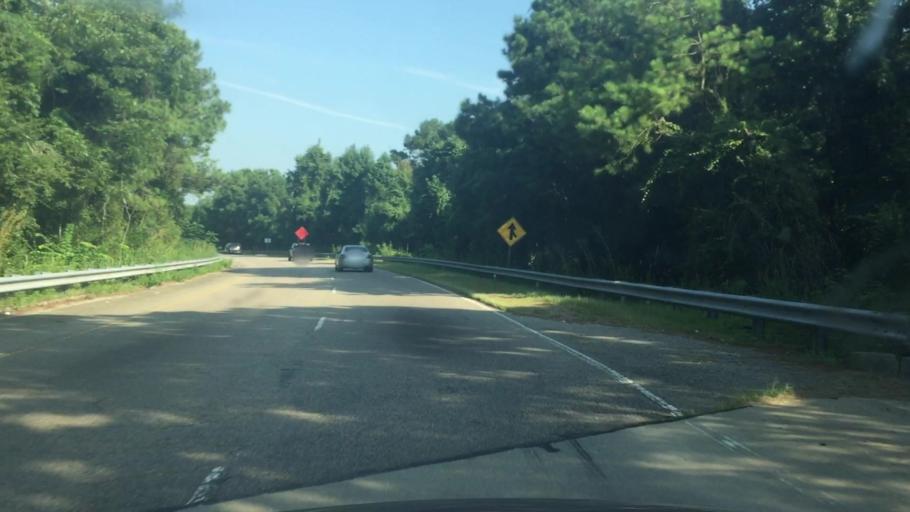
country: US
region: South Carolina
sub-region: Horry County
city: Little River
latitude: 33.8635
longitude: -78.6575
